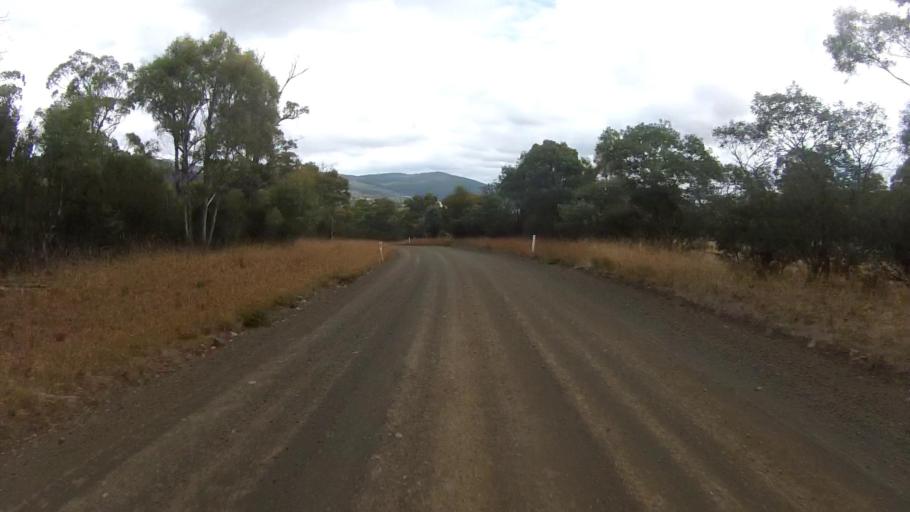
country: AU
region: Tasmania
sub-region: Break O'Day
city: St Helens
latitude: -41.8205
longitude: 147.9908
